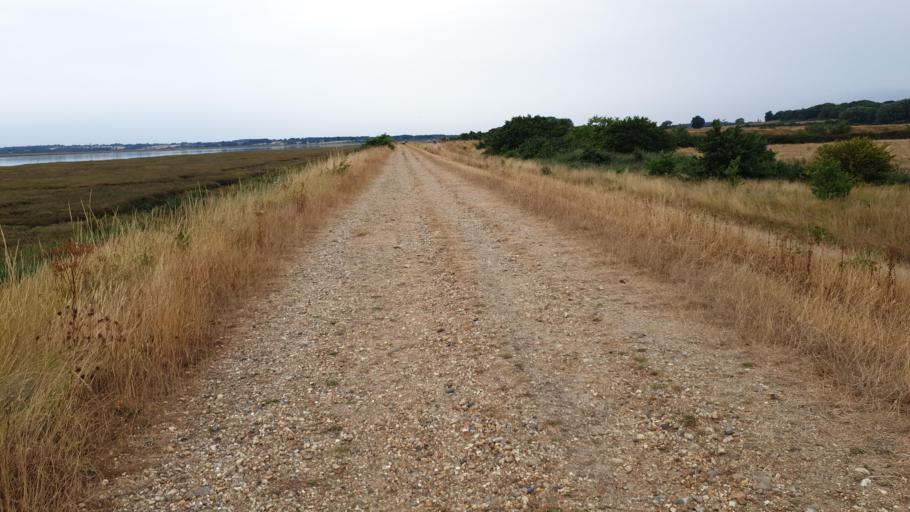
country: GB
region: England
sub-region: Essex
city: Brightlingsea
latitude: 51.8145
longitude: 0.9987
